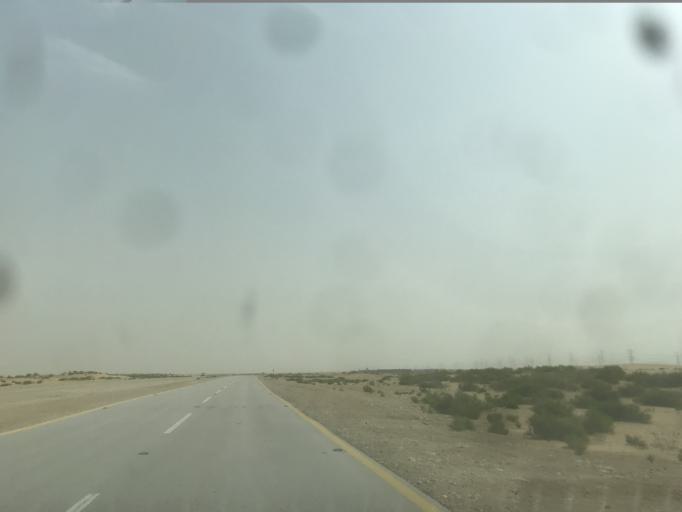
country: SA
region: Eastern Province
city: Abqaiq
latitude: 25.9175
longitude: 49.8484
